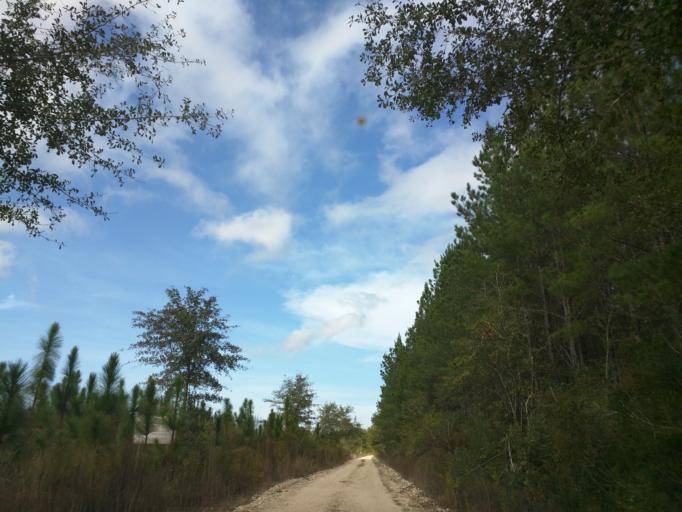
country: US
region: Florida
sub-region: Escambia County
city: Cantonment
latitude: 30.5347
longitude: -87.4368
